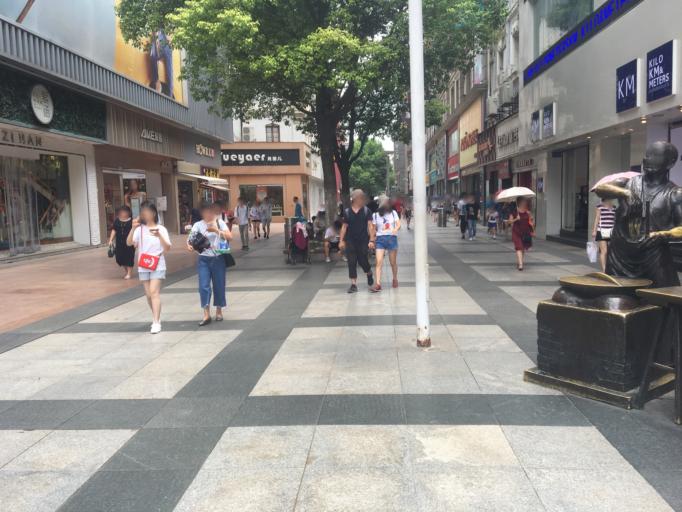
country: CN
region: Hubei
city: Wuhan
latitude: 30.5810
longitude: 114.2890
